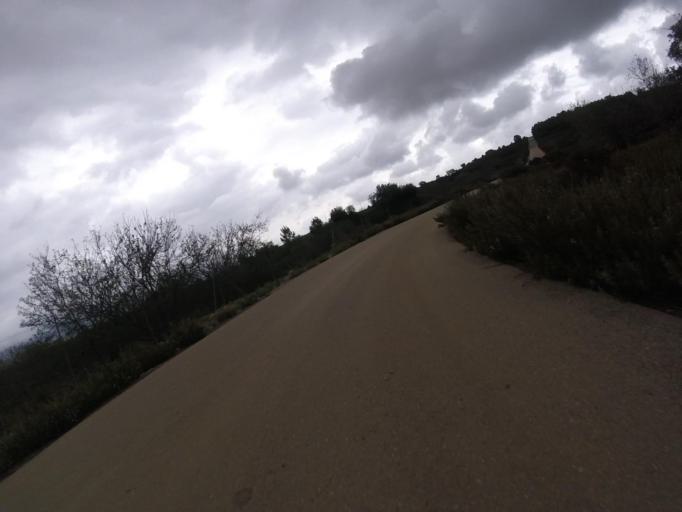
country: ES
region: Valencia
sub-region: Provincia de Castello
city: Benlloch
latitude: 40.2055
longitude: 0.0714
